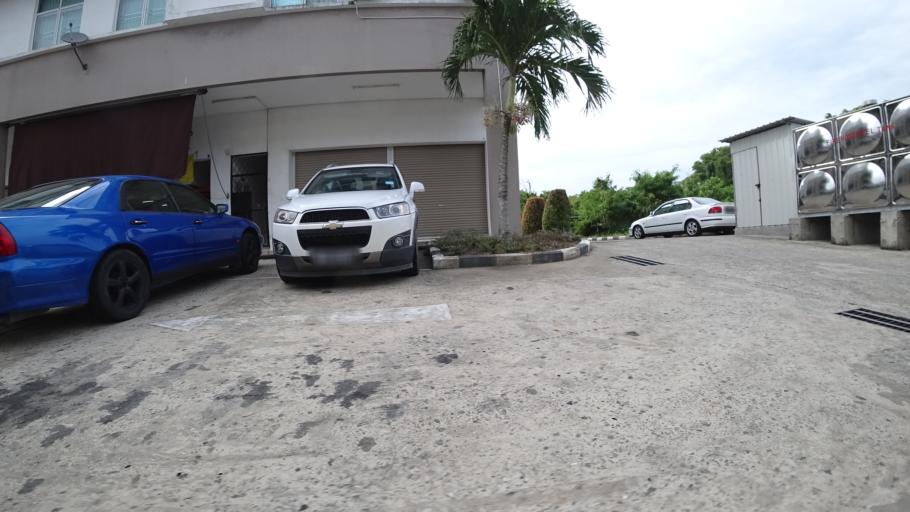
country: BN
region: Brunei and Muara
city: Bandar Seri Begawan
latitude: 4.9071
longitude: 114.9237
